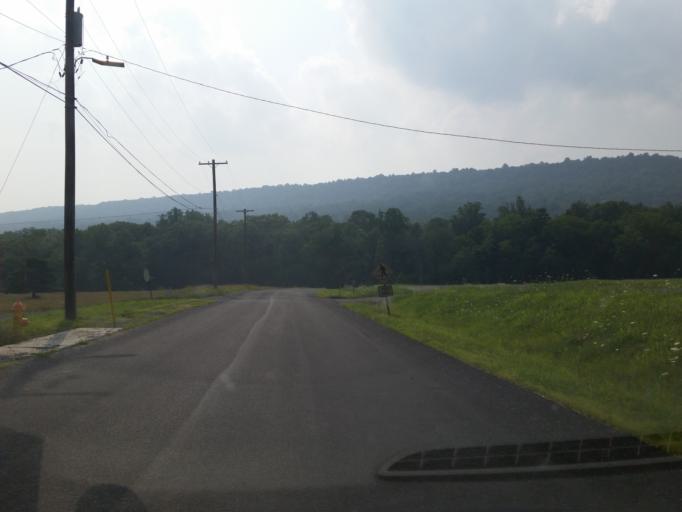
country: US
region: Pennsylvania
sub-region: Lebanon County
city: Jonestown
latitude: 40.4293
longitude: -76.5949
